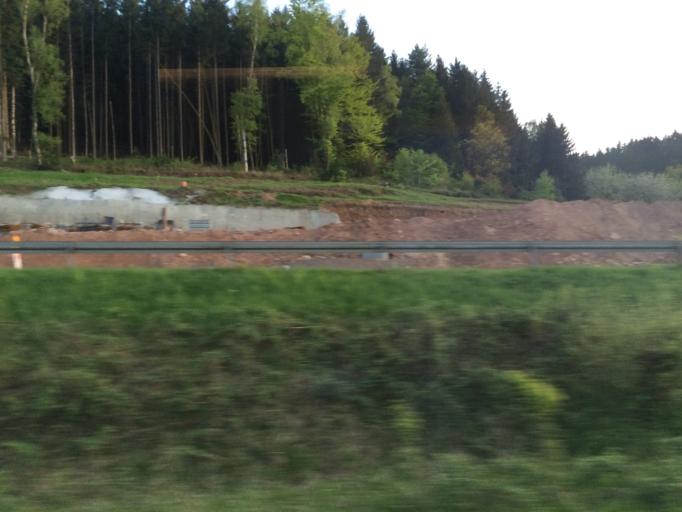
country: DE
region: Bavaria
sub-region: Regierungsbezirk Unterfranken
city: Heigenbrucken
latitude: 50.0218
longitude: 9.3824
